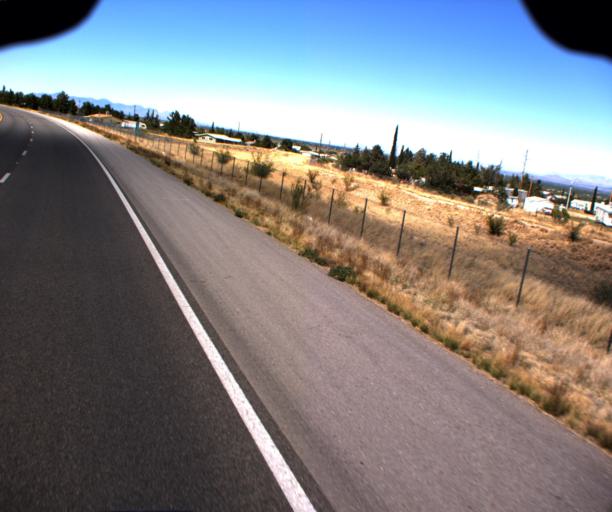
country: US
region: Arizona
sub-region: Cochise County
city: Sierra Vista Southeast
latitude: 31.4316
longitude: -110.2415
